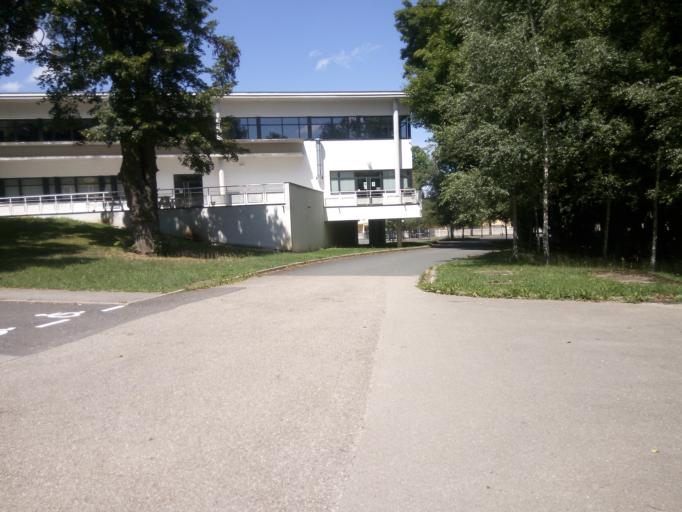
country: FR
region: Lorraine
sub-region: Departement de Meurthe-et-Moselle
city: Villers-les-Nancy
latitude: 48.6674
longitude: 6.1550
